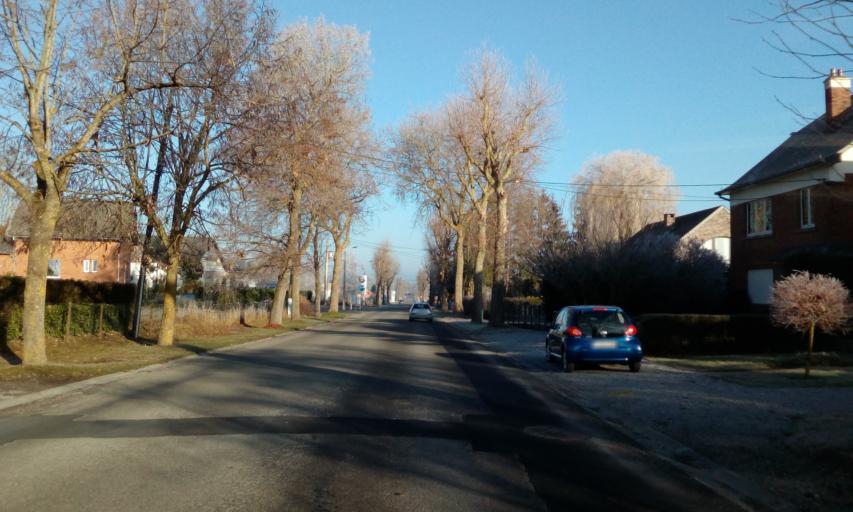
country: BE
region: Wallonia
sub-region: Province de Namur
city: Couvin
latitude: 50.0819
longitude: 4.5155
